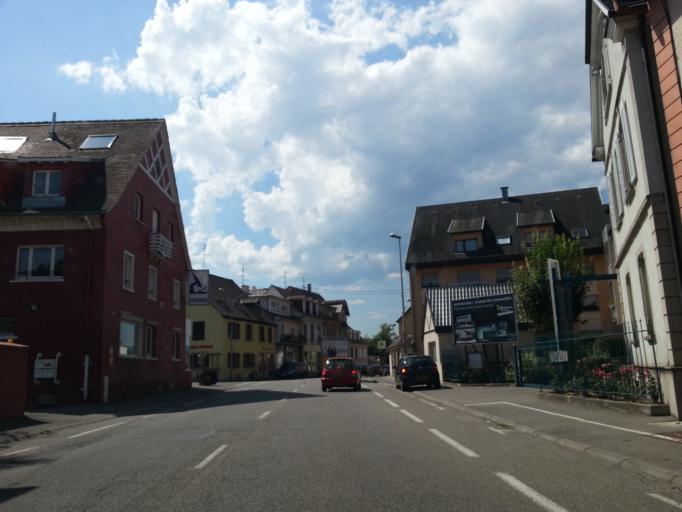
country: FR
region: Alsace
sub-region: Departement du Haut-Rhin
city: Horbourg-Wihr
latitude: 48.0808
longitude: 7.3957
